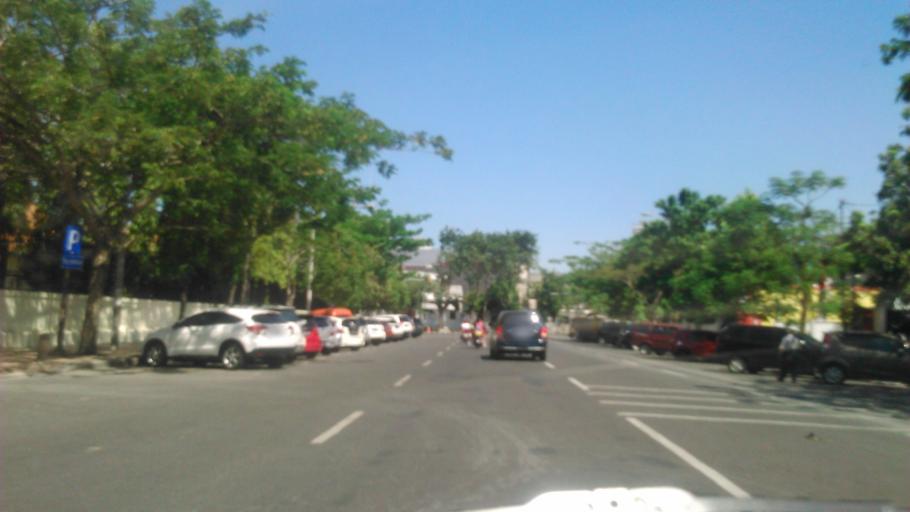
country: ID
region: East Java
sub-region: Kota Surabaya
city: Surabaya
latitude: -7.2572
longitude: 112.7490
